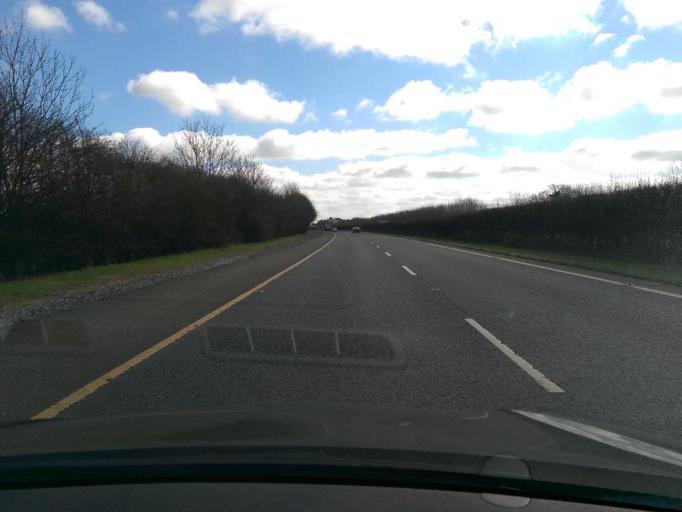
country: IE
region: Leinster
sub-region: Kildare
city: Kilcock
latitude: 53.3827
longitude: -6.6583
